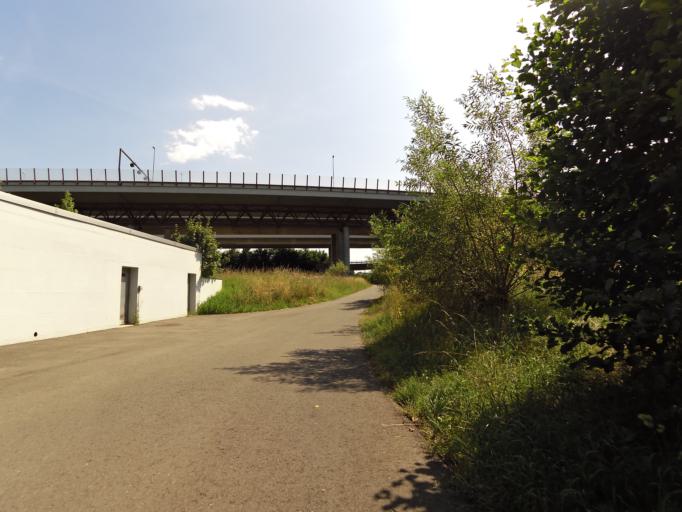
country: CH
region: Aargau
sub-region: Bezirk Baden
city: Baden
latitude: 47.4593
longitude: 8.2864
